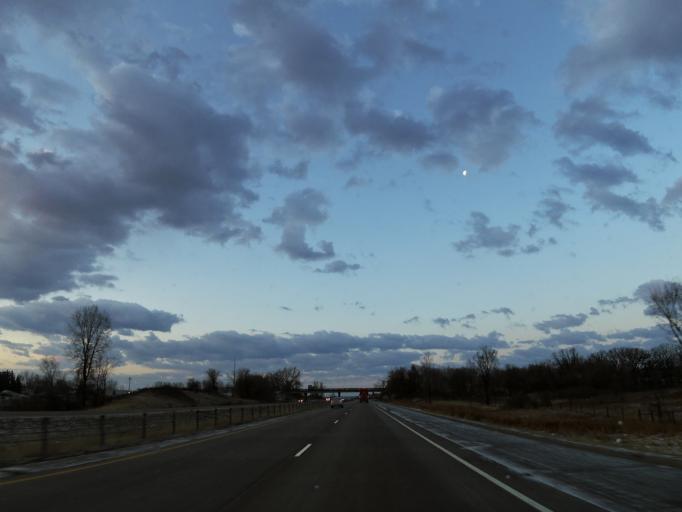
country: US
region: Minnesota
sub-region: Dakota County
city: Lakeville
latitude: 44.6264
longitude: -93.2985
